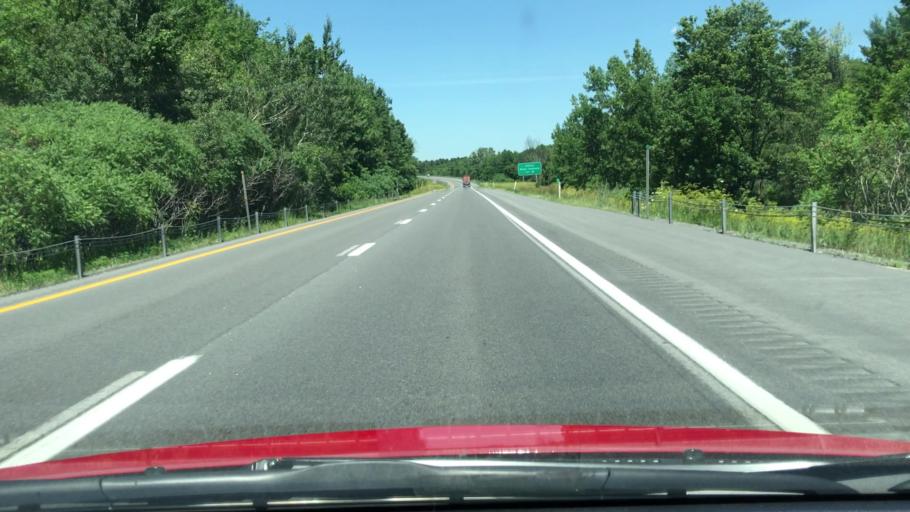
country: US
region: New York
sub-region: Clinton County
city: Champlain
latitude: 44.8761
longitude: -73.4512
